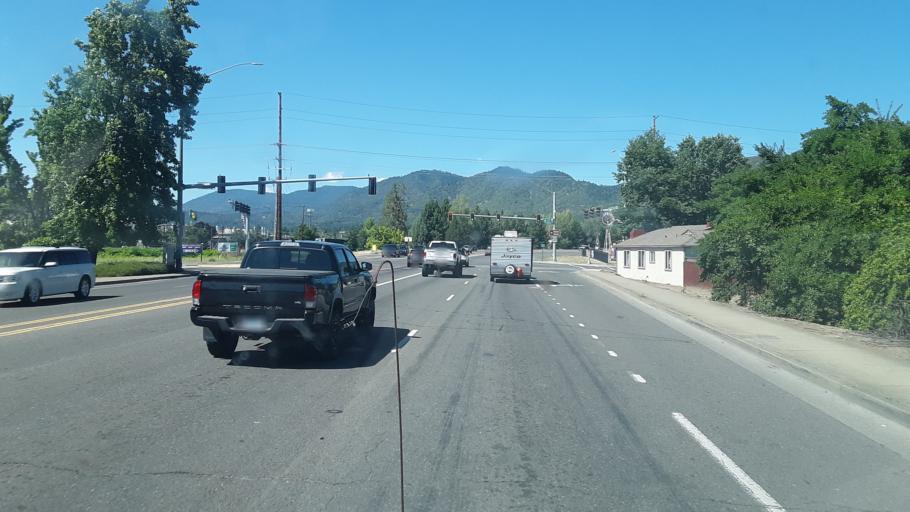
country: US
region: Oregon
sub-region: Josephine County
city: Fruitdale
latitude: 42.4298
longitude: -123.3183
